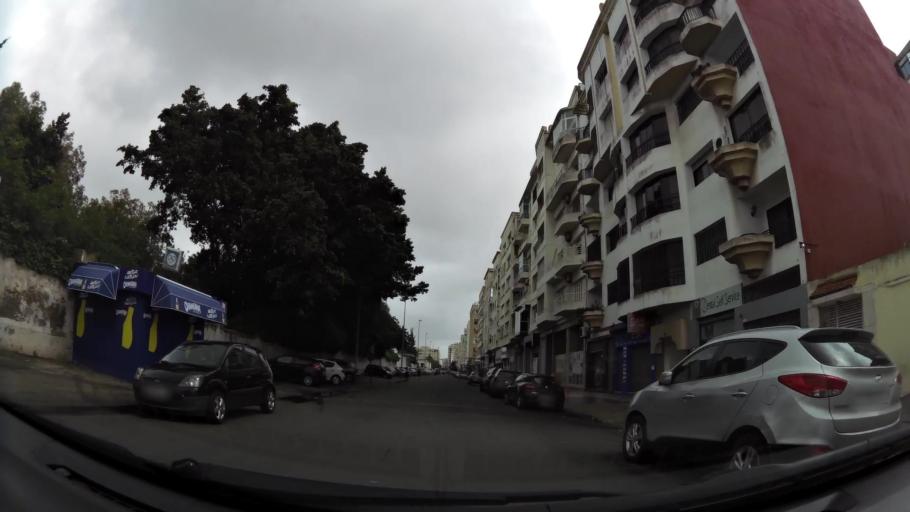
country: MA
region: Grand Casablanca
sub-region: Casablanca
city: Casablanca
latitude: 33.5727
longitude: -7.6222
